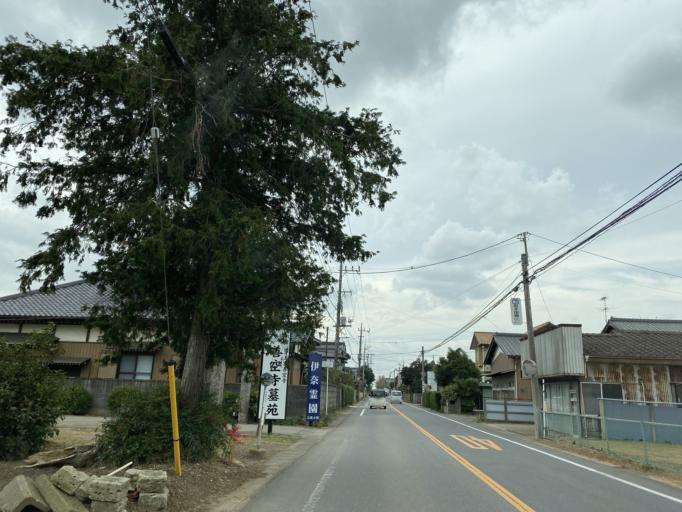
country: JP
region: Ibaraki
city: Moriya
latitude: 35.9836
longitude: 140.0427
